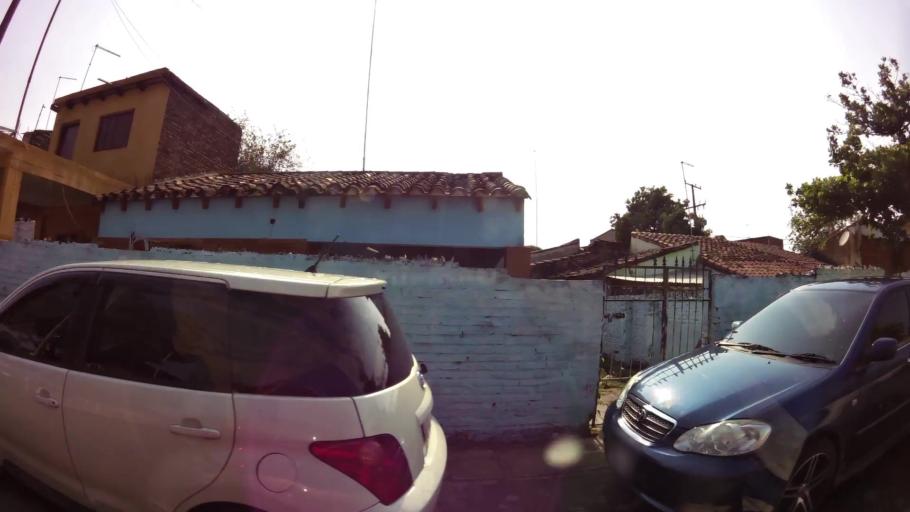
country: PY
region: Asuncion
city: Asuncion
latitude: -25.3000
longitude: -57.6658
